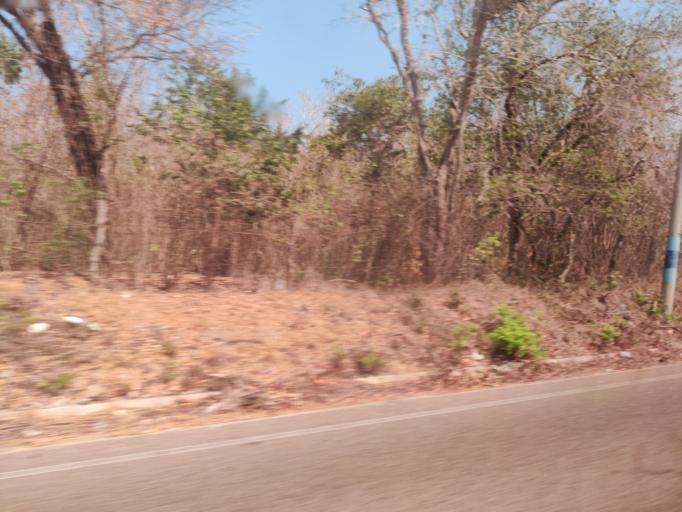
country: CO
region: Bolivar
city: Turbana
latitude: 10.2200
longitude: -75.5846
